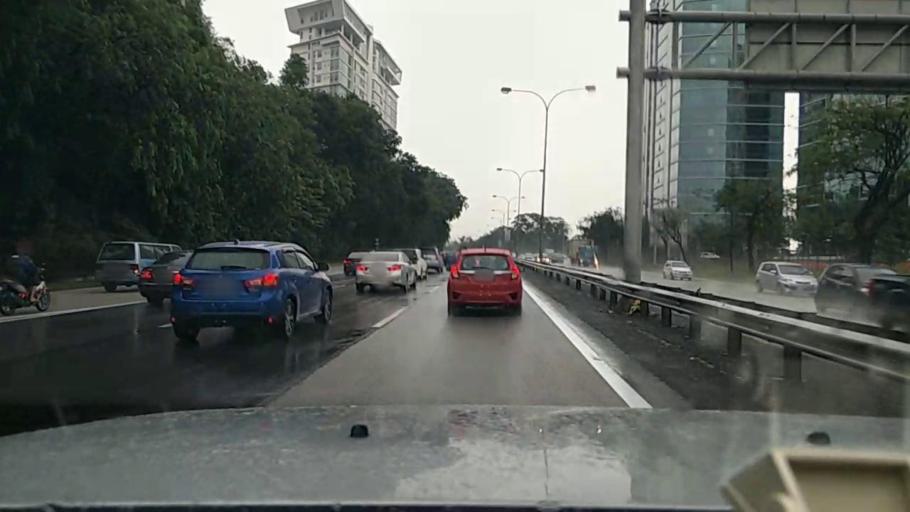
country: MY
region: Kuala Lumpur
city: Kuala Lumpur
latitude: 3.1055
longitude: 101.6936
